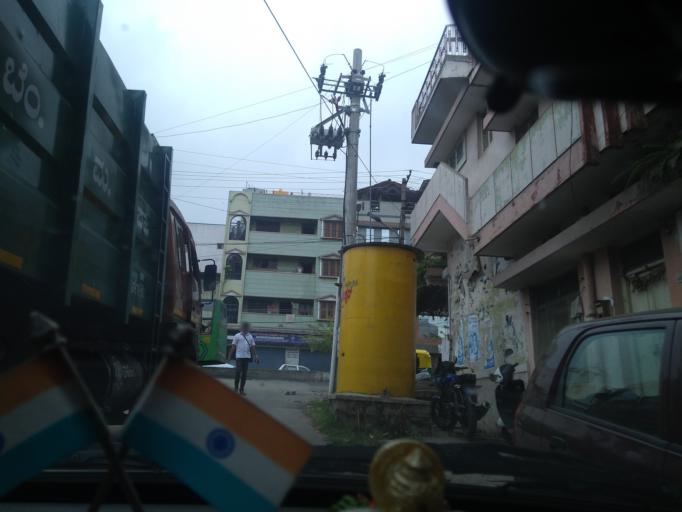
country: IN
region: Karnataka
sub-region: Bangalore Urban
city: Bangalore
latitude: 12.9763
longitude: 77.5530
